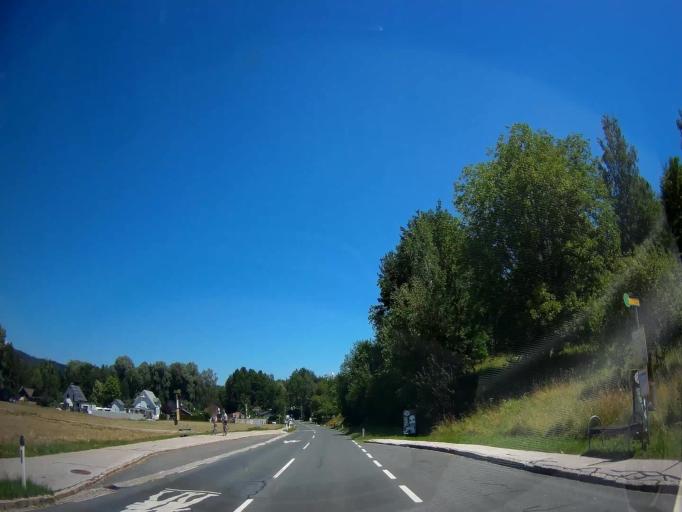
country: AT
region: Carinthia
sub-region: Politischer Bezirk Klagenfurt Land
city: Kottmannsdorf
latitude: 46.6071
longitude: 14.2568
